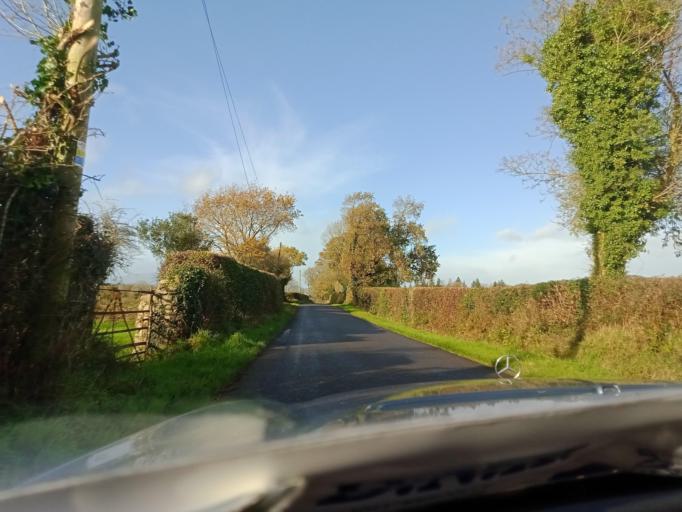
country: IE
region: Leinster
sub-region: Kilkenny
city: Mooncoin
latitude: 52.3311
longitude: -7.2562
